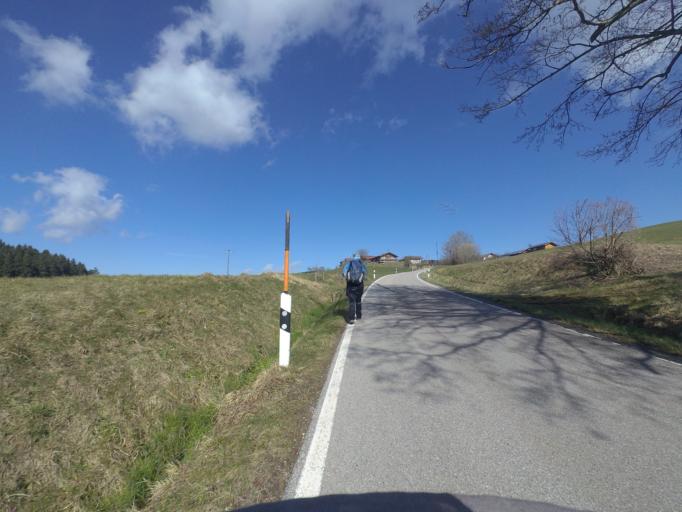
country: DE
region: Bavaria
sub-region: Upper Bavaria
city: Piding
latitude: 47.7896
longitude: 12.9006
